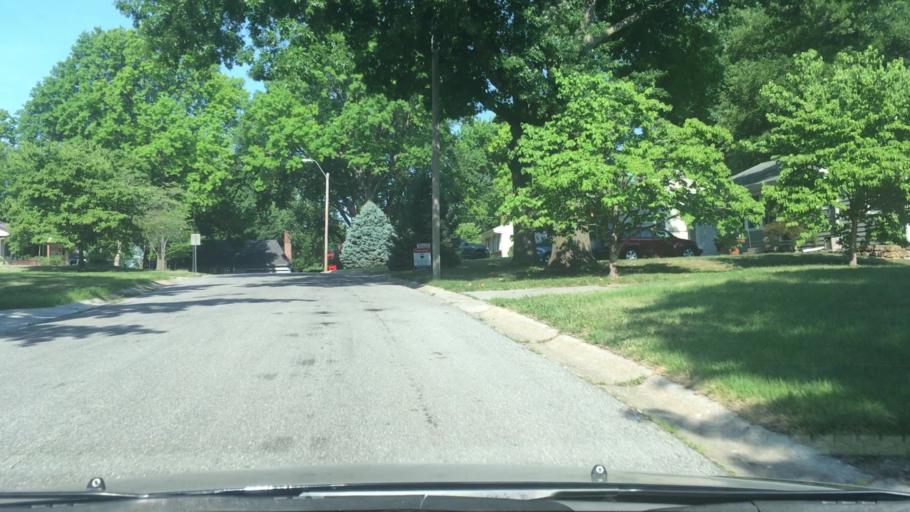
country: US
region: Kansas
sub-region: Johnson County
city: Leawood
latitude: 38.9655
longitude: -94.5999
